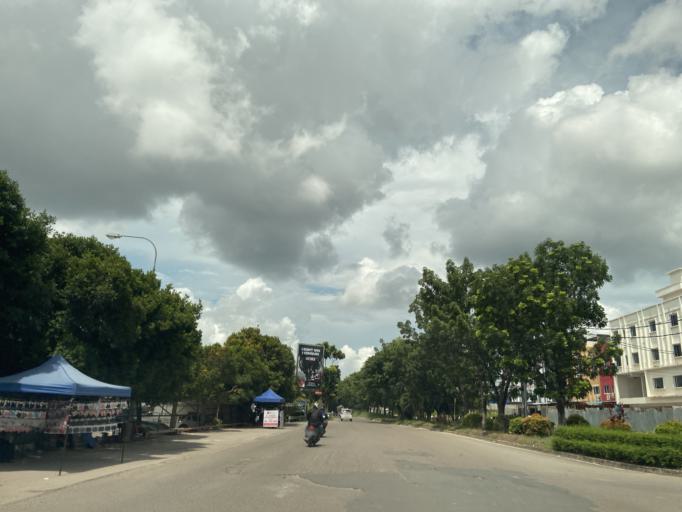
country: SG
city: Singapore
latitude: 1.1381
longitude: 104.0013
